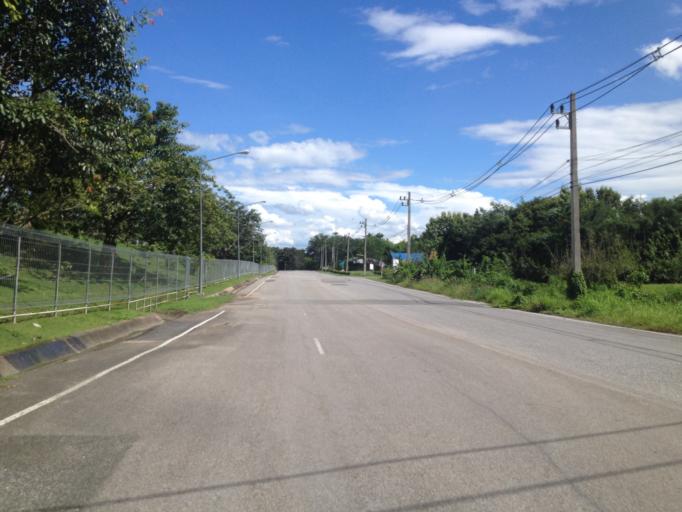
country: TH
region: Chiang Mai
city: Hang Dong
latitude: 18.7466
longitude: 98.9213
